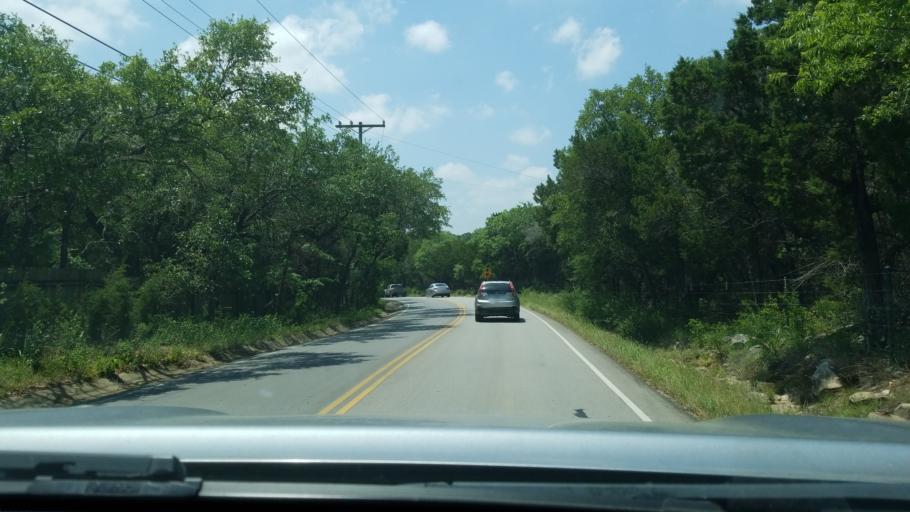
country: US
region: Texas
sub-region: Hays County
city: Woodcreek
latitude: 30.0345
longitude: -98.1198
